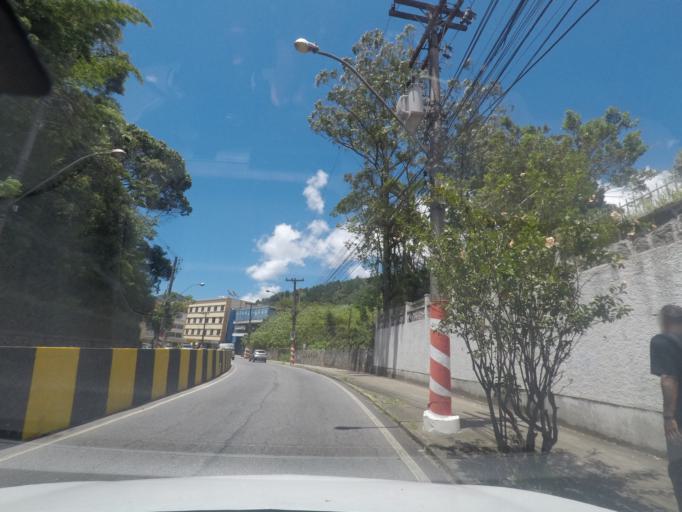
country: BR
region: Rio de Janeiro
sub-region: Teresopolis
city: Teresopolis
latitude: -22.4270
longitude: -42.9806
